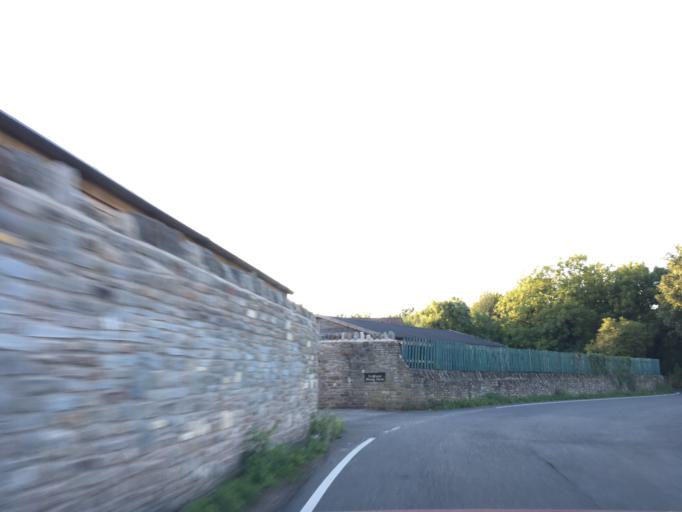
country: GB
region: England
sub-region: Bath and North East Somerset
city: Whitchurch
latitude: 51.4254
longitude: -2.5360
